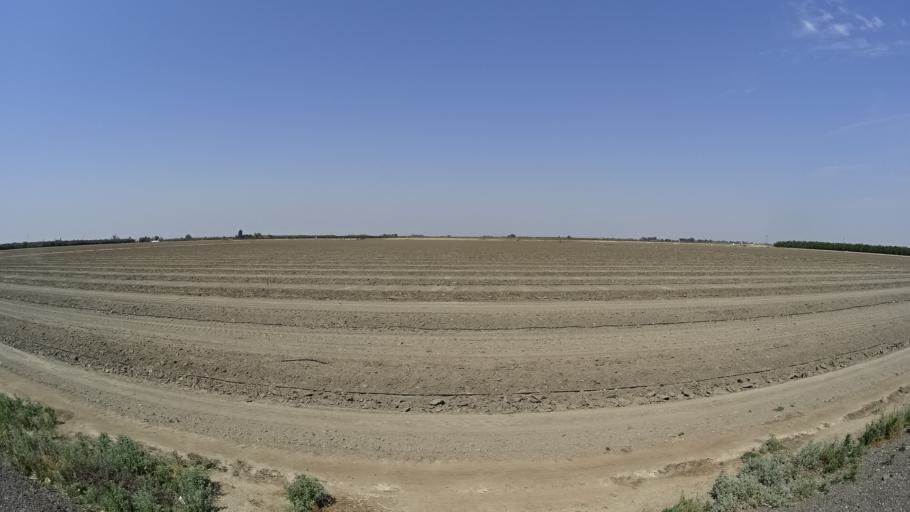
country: US
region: California
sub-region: Kings County
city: Armona
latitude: 36.3475
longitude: -119.7448
